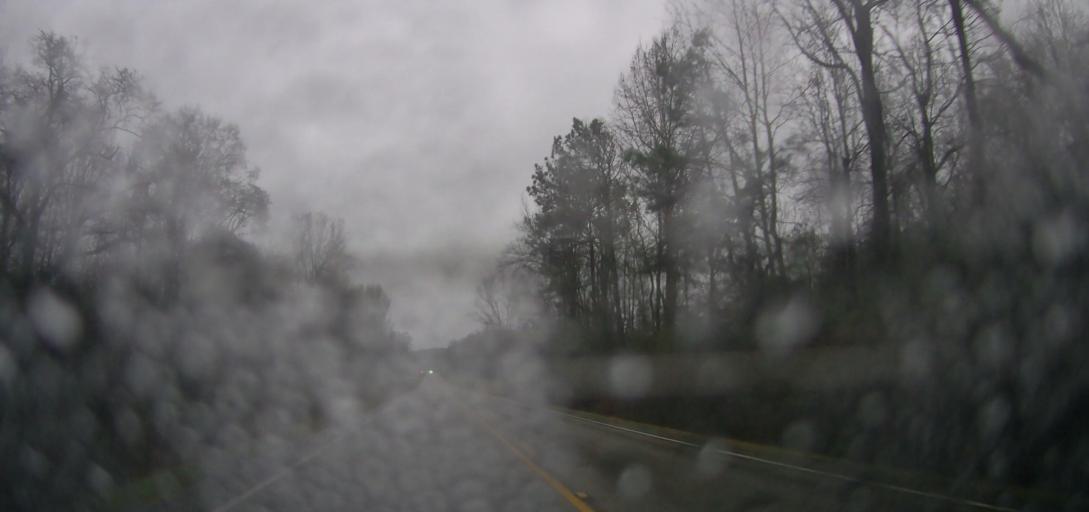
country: US
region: Alabama
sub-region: Autauga County
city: Prattville
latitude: 32.5097
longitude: -86.5875
